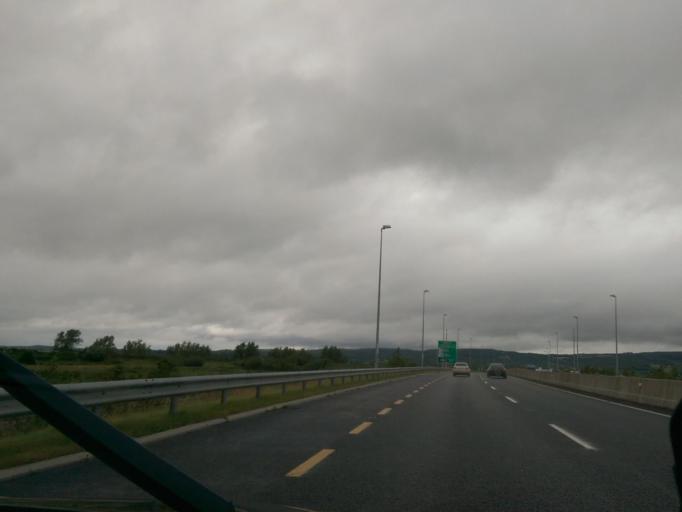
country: IE
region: Munster
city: Moyross
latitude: 52.6639
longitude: -8.6972
